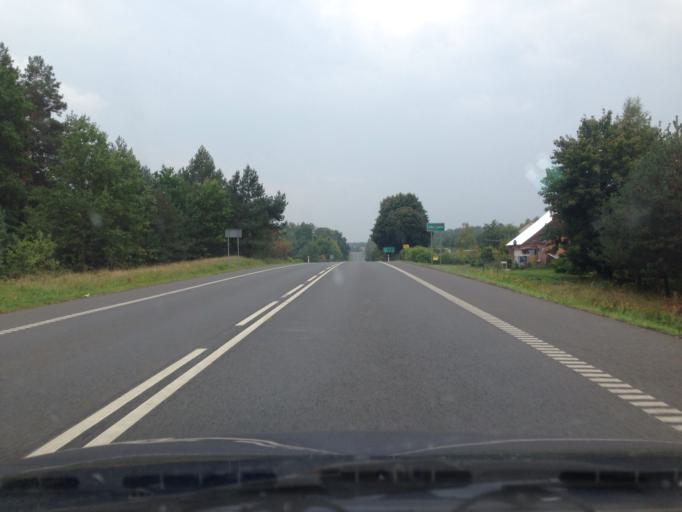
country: PL
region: Kujawsko-Pomorskie
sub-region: Powiat swiecki
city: Nowe
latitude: 53.6279
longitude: 18.6763
